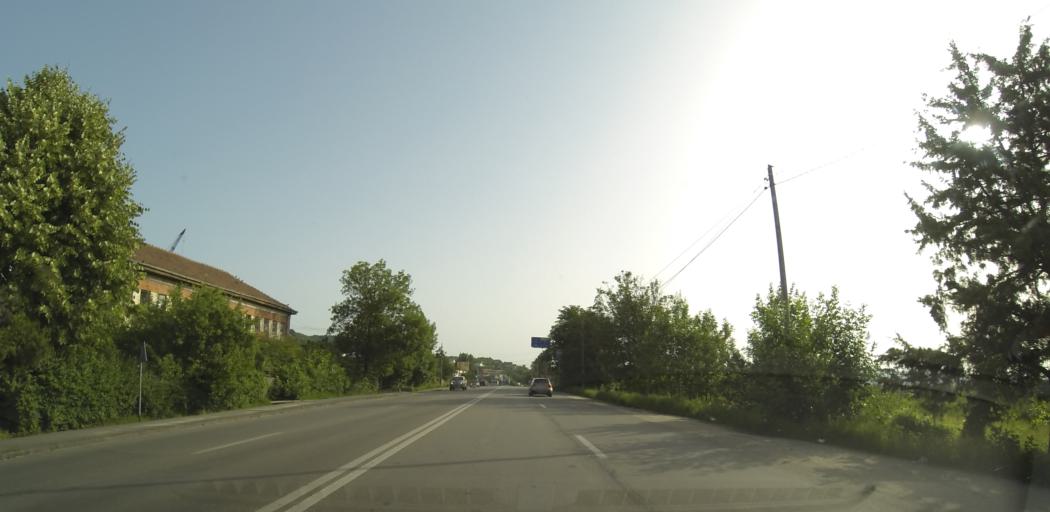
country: RO
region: Valcea
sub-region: Municipiul Ramnicu Valcea
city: Ramnicu Valcea
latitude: 45.0773
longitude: 24.3504
